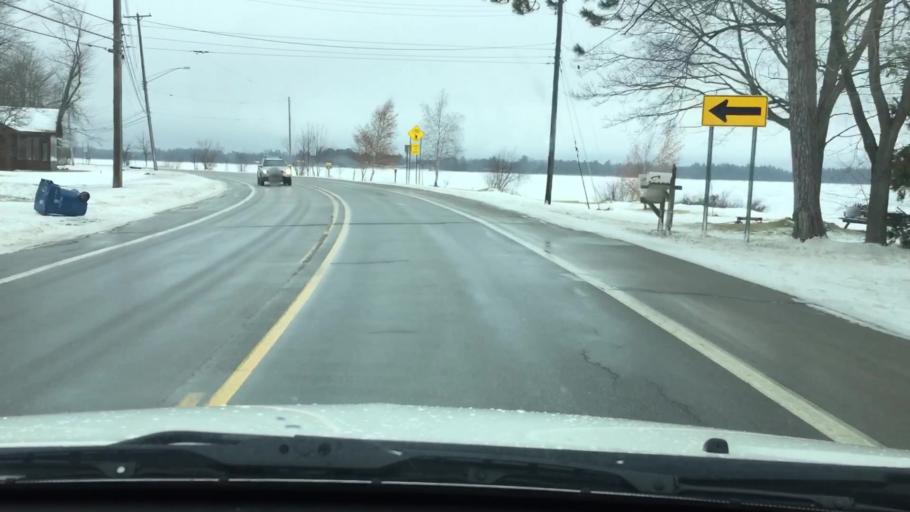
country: US
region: Michigan
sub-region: Wexford County
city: Cadillac
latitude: 44.2347
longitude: -85.4320
